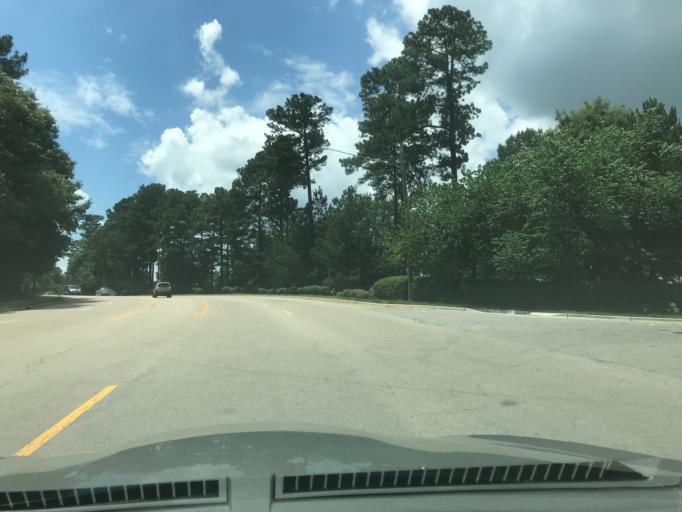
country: US
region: North Carolina
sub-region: Wake County
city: Raleigh
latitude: 35.8354
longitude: -78.6074
